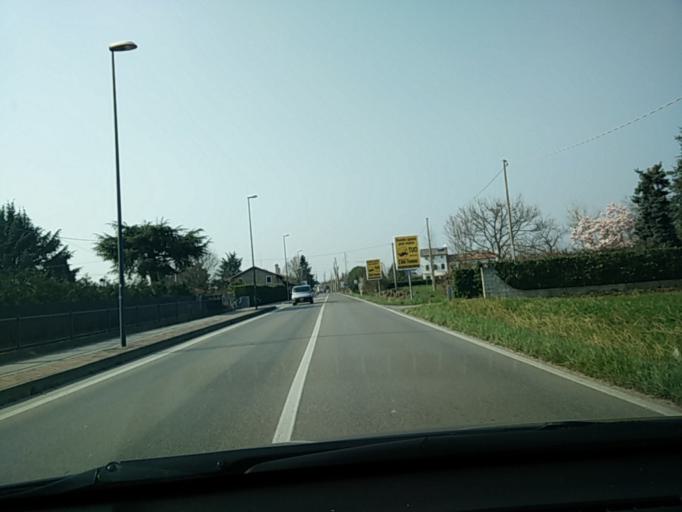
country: IT
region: Veneto
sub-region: Provincia di Treviso
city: Postioma
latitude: 45.7122
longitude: 12.1629
